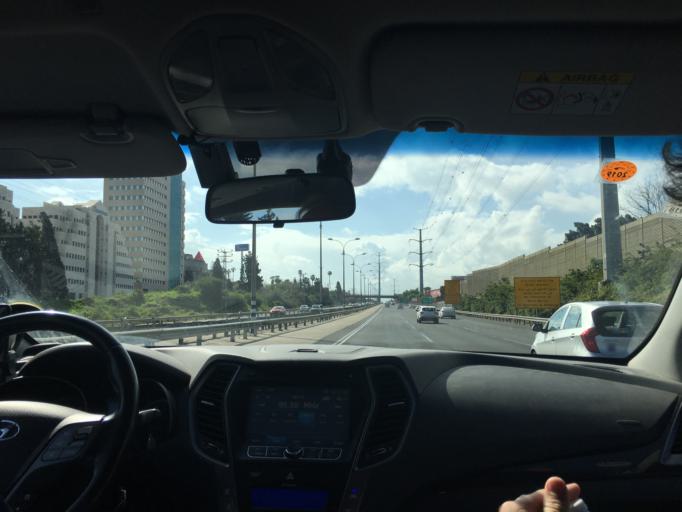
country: IL
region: Tel Aviv
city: Giv`at Shemu'el
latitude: 32.0817
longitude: 34.8450
